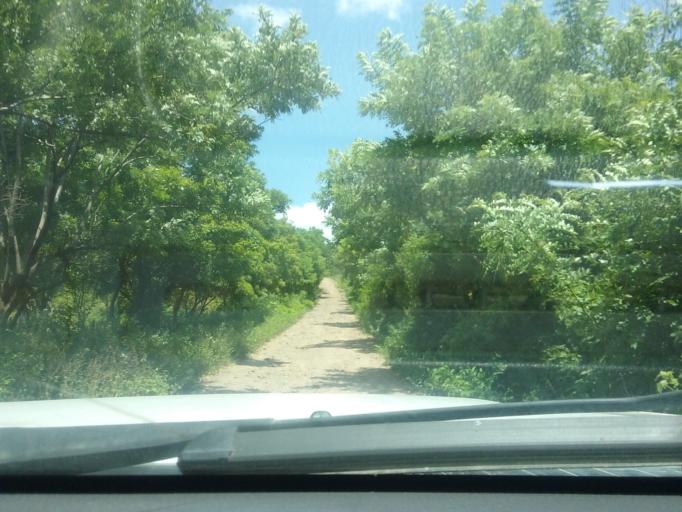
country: NI
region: Matagalpa
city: Terrabona
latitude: 12.6794
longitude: -85.9711
